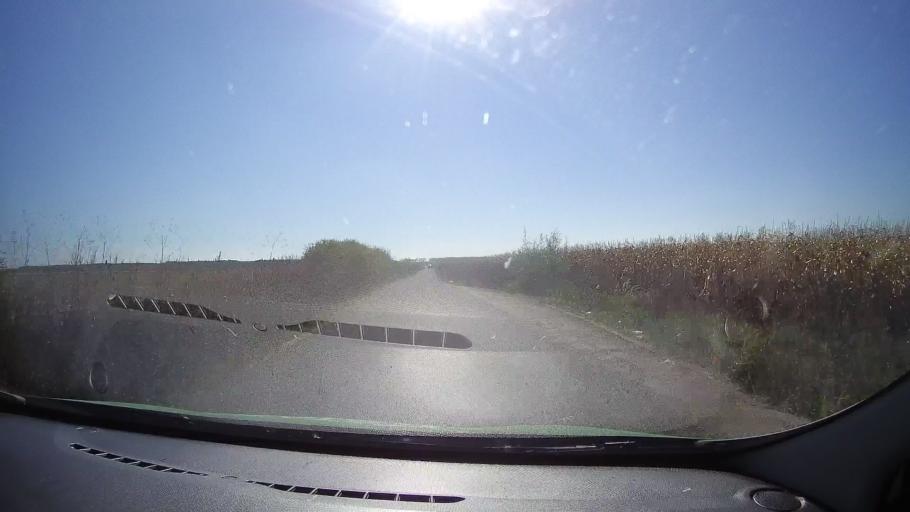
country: RO
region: Satu Mare
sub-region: Comuna Doba
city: Doba
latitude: 47.7312
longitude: 22.7242
